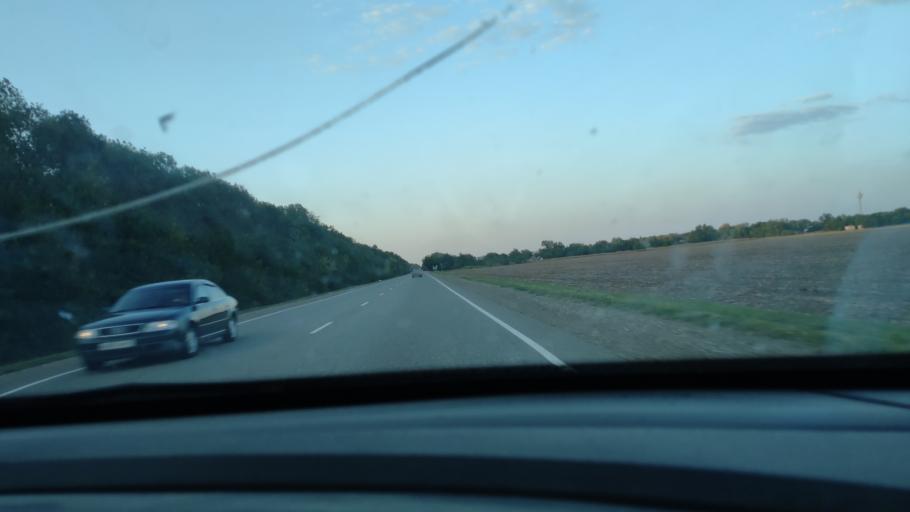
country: RU
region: Krasnodarskiy
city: Novominskaya
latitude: 46.4054
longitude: 39.0002
